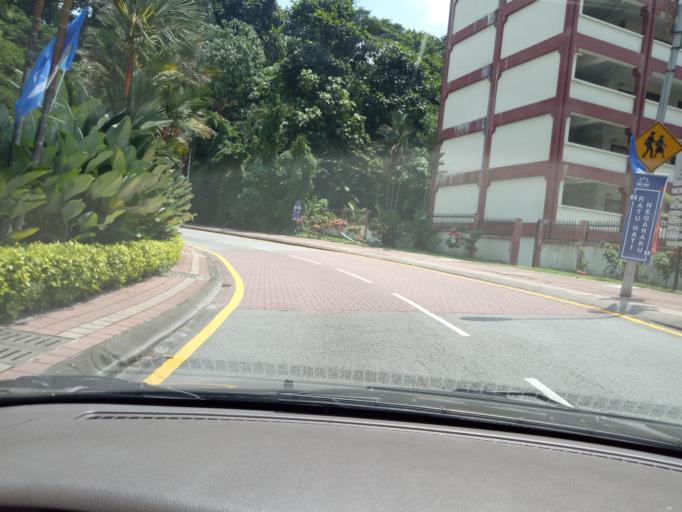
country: MY
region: Kuala Lumpur
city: Kuala Lumpur
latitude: 3.1702
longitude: 101.6911
